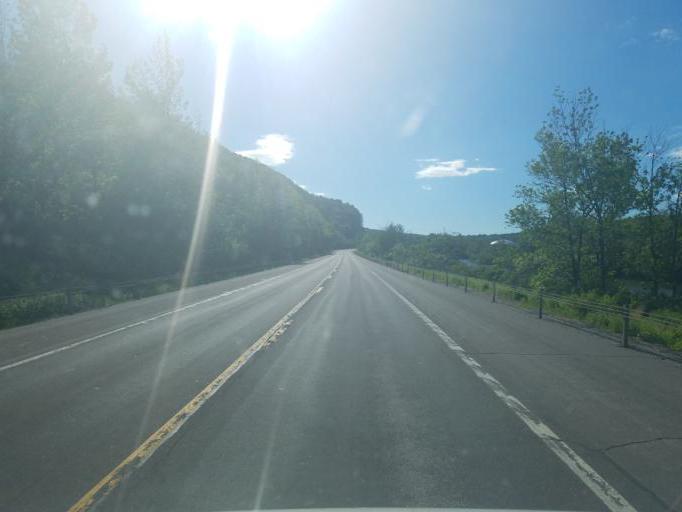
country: US
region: New York
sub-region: Herkimer County
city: Little Falls
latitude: 43.0354
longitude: -74.8372
